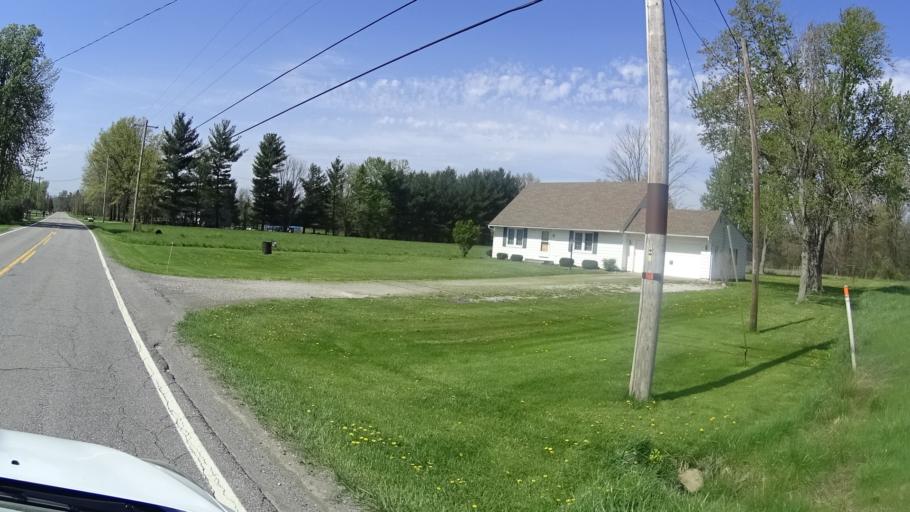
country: US
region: Ohio
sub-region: Lorain County
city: Lagrange
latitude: 41.2880
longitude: -82.1452
